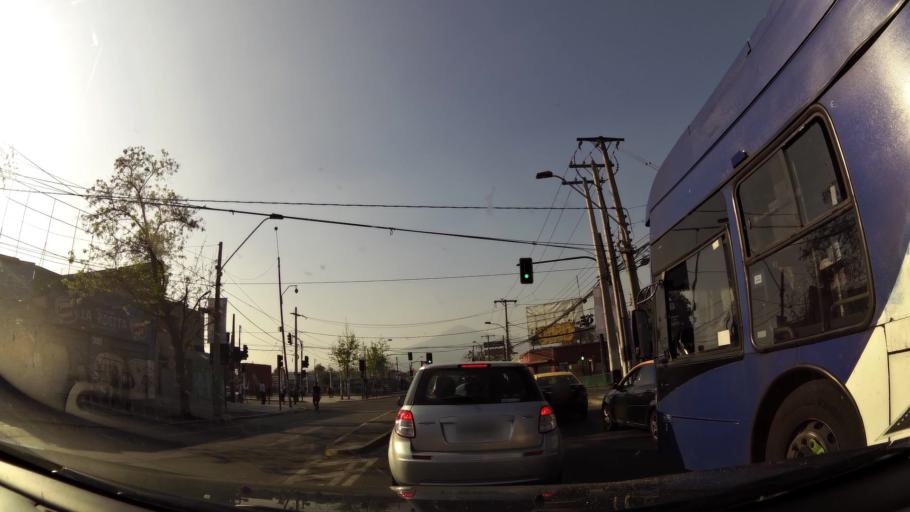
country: CL
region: Santiago Metropolitan
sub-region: Provincia de Santiago
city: Santiago
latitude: -33.3973
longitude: -70.6428
